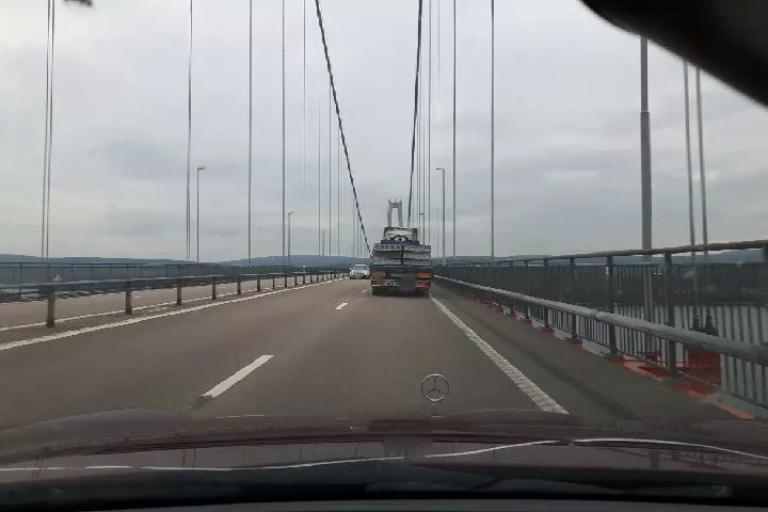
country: SE
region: Vaesternorrland
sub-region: Haernoesands Kommun
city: Haernoesand
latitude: 62.7994
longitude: 17.9406
